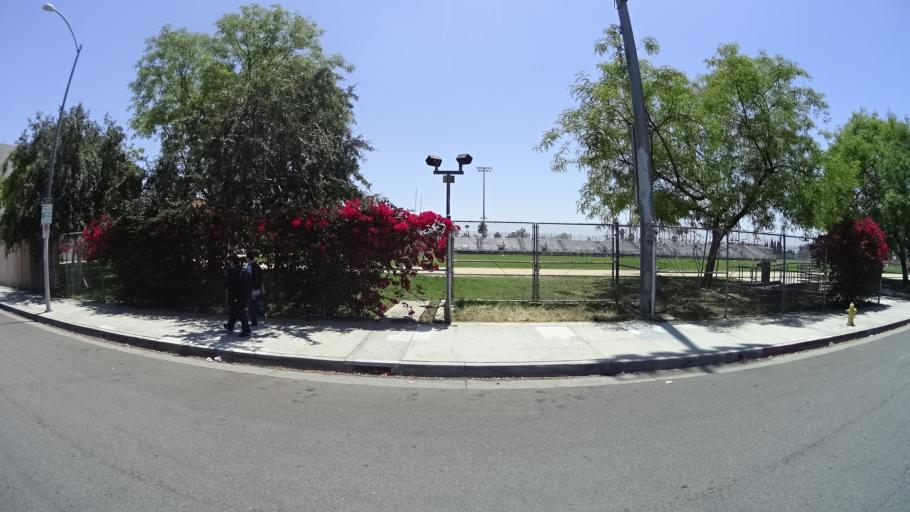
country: US
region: California
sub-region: Los Angeles County
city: Van Nuys
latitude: 34.2179
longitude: -118.4510
